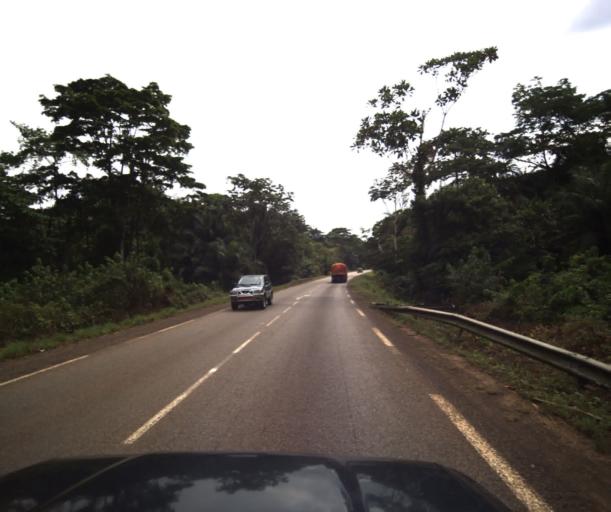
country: CM
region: Littoral
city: Edea
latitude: 3.8386
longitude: 10.4643
